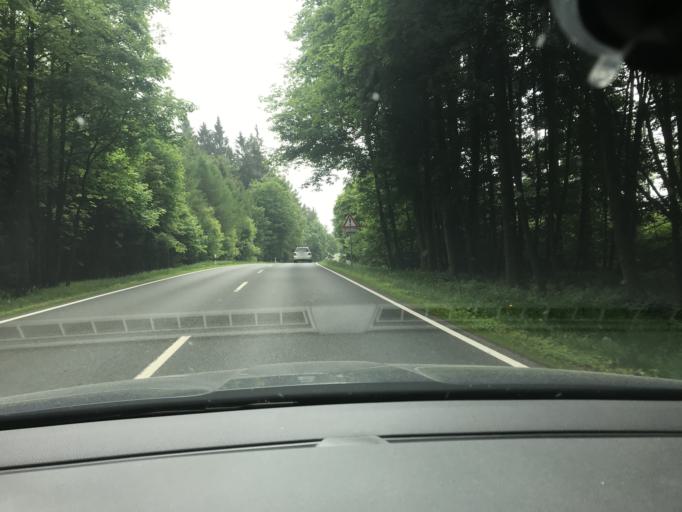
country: DE
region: Saxony
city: Brand-Erbisdorf
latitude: 50.8334
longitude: 13.3240
